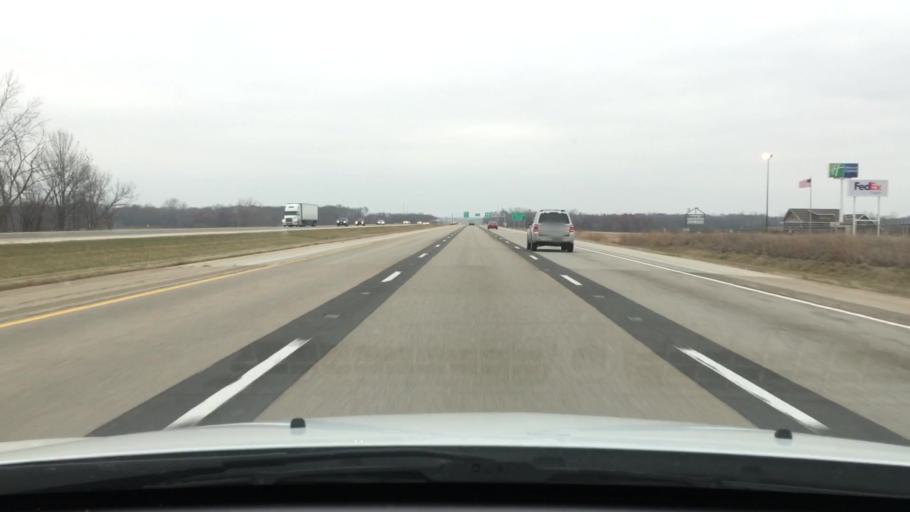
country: US
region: Illinois
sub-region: Logan County
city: Lincoln
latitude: 40.1552
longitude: -89.4173
